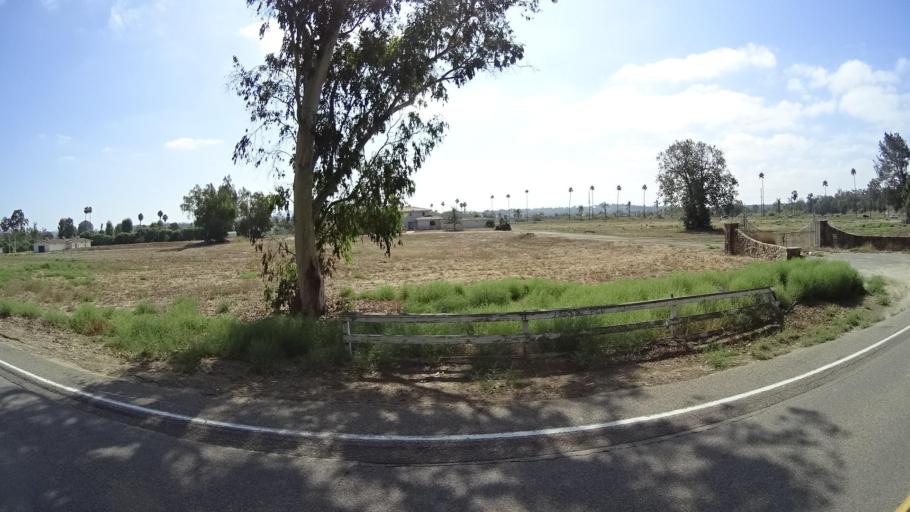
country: US
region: California
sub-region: San Diego County
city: Rancho Santa Fe
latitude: 33.0073
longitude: -117.2072
